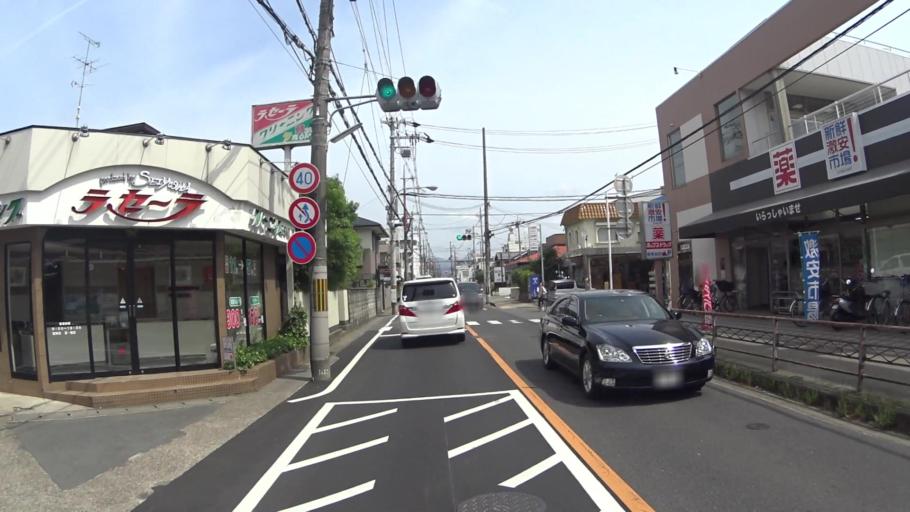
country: JP
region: Kyoto
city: Muko
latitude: 34.9697
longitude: 135.6940
